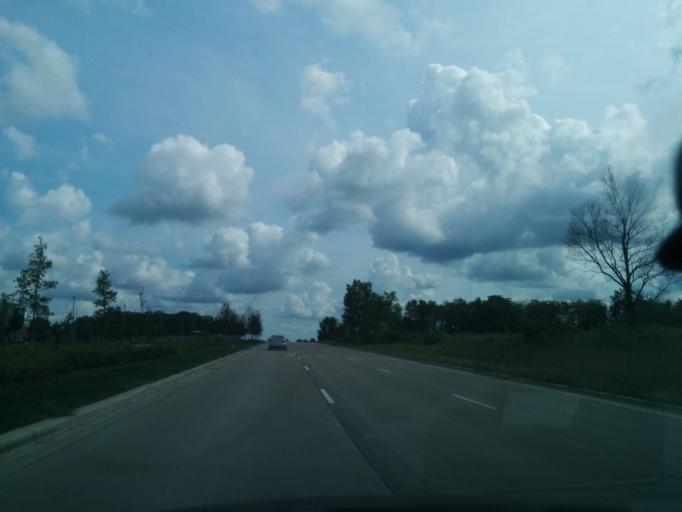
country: US
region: Illinois
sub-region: Cook County
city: Orland Hills
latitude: 41.5746
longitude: -87.8519
